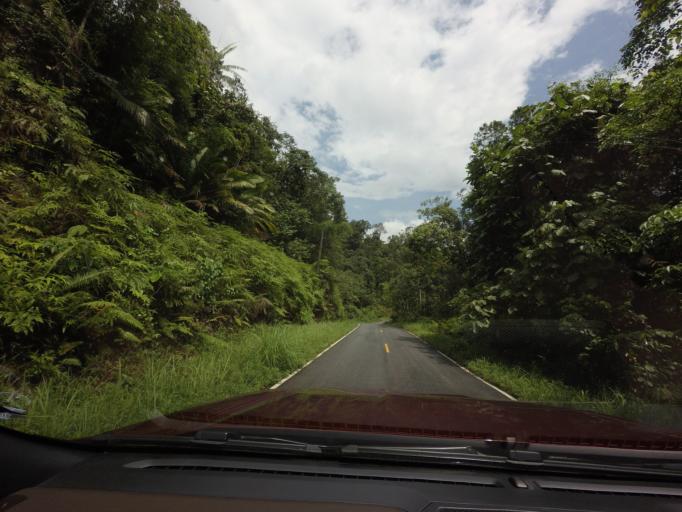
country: TH
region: Narathiwat
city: Sukhirin
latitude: 5.9423
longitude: 101.6525
